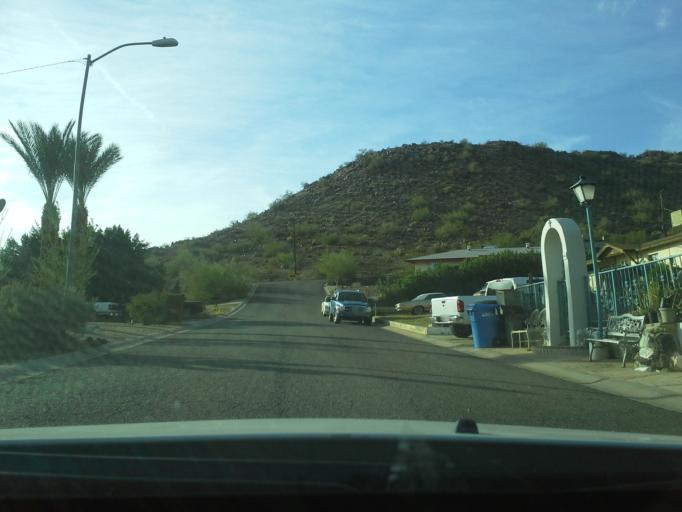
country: US
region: Arizona
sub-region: Maricopa County
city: Glendale
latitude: 33.5840
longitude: -112.0850
